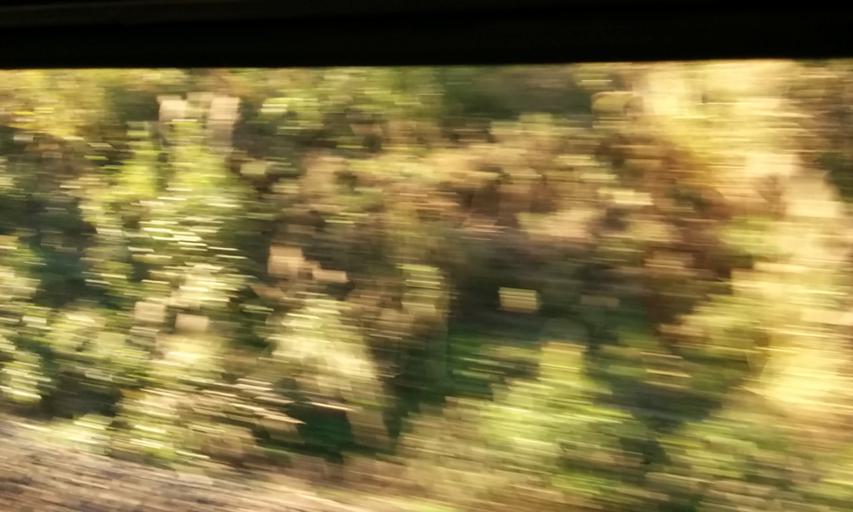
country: JP
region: Gifu
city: Mizunami
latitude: 35.4006
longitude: 137.2956
